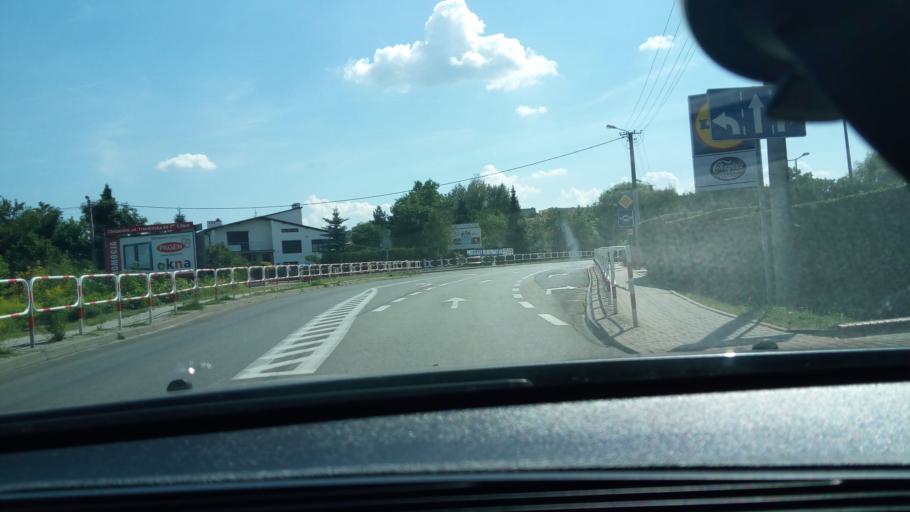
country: PL
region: Lesser Poland Voivodeship
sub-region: Powiat chrzanowski
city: Chrzanow
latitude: 50.1363
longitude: 19.4089
